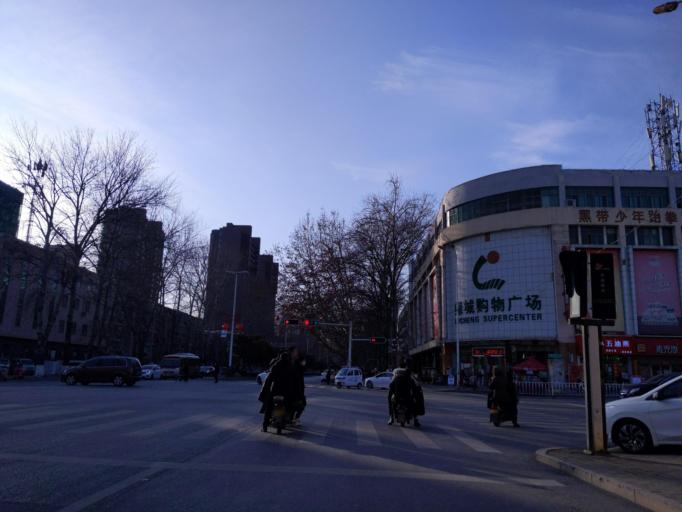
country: CN
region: Henan Sheng
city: Puyang
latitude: 35.7620
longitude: 115.0140
